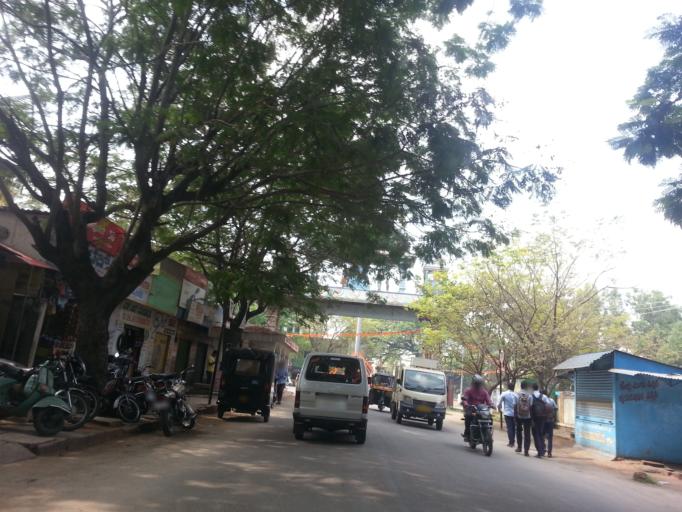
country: IN
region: Karnataka
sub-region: Mysore
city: Mysore
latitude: 12.3321
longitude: 76.6624
